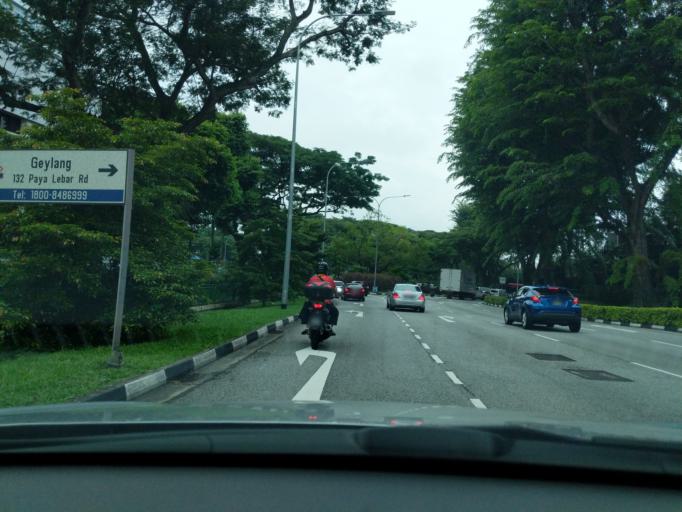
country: SG
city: Singapore
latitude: 1.3229
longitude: 103.8921
